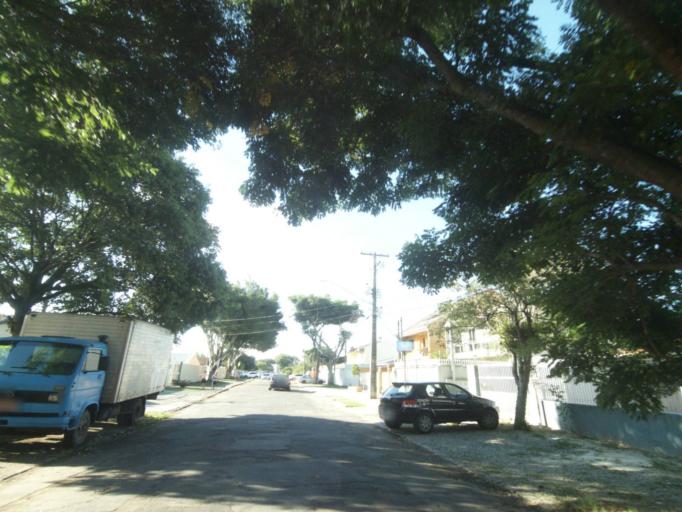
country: BR
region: Parana
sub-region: Pinhais
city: Pinhais
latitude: -25.4531
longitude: -49.2057
